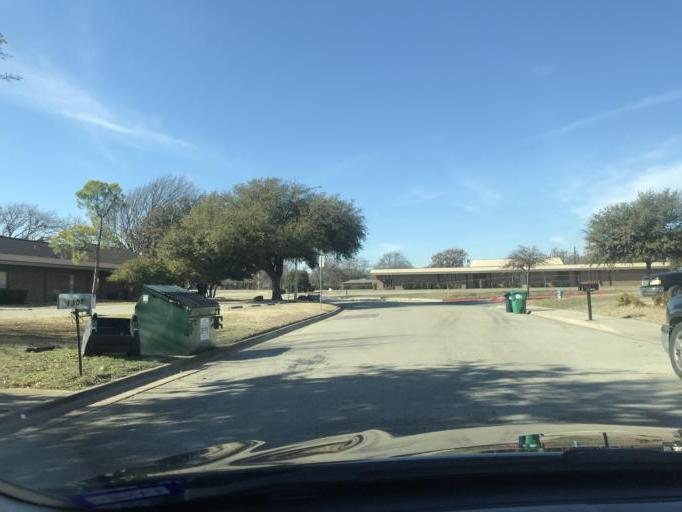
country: US
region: Texas
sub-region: Denton County
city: Denton
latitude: 33.2267
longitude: -97.1477
